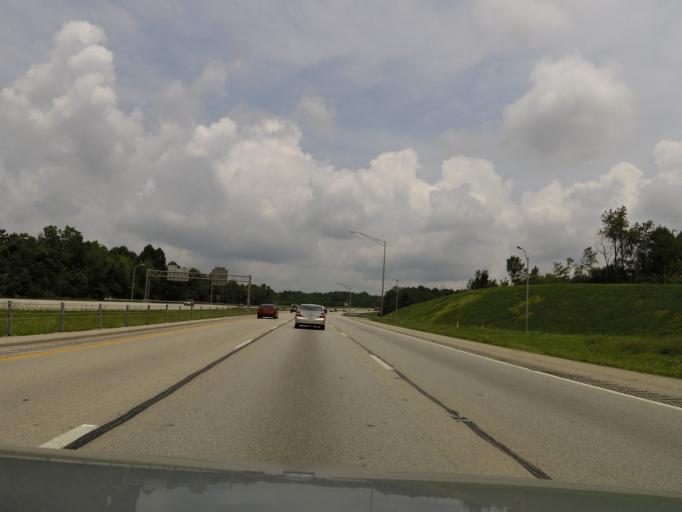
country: US
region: Kentucky
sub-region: Hardin County
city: Elizabethtown
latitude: 37.7153
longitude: -85.8291
